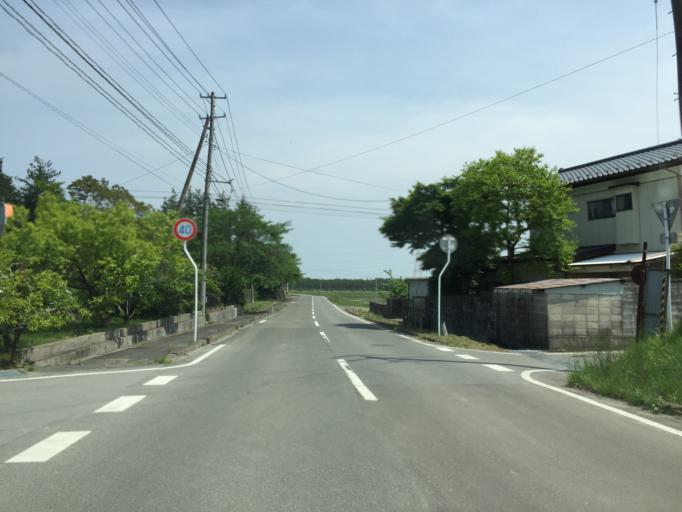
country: JP
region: Miyagi
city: Marumori
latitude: 37.8454
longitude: 140.9289
